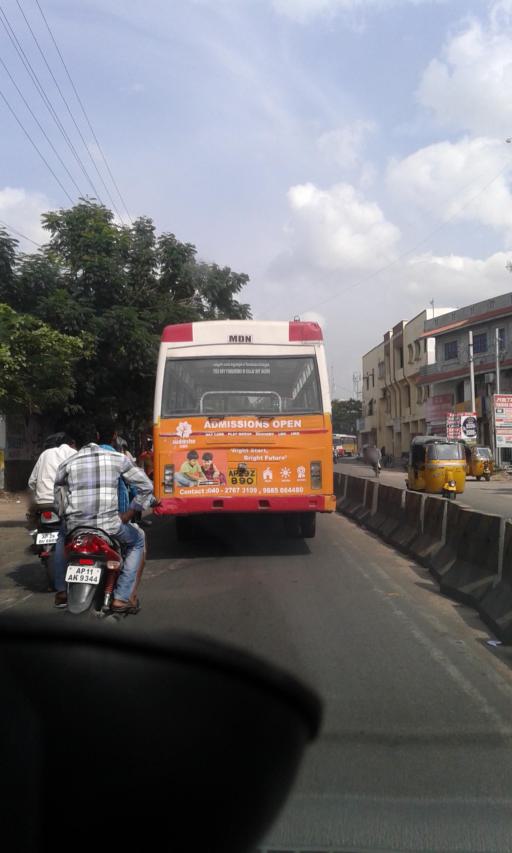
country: IN
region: Telangana
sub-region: Rangareddi
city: Gaddi Annaram
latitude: 17.3636
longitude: 78.5026
